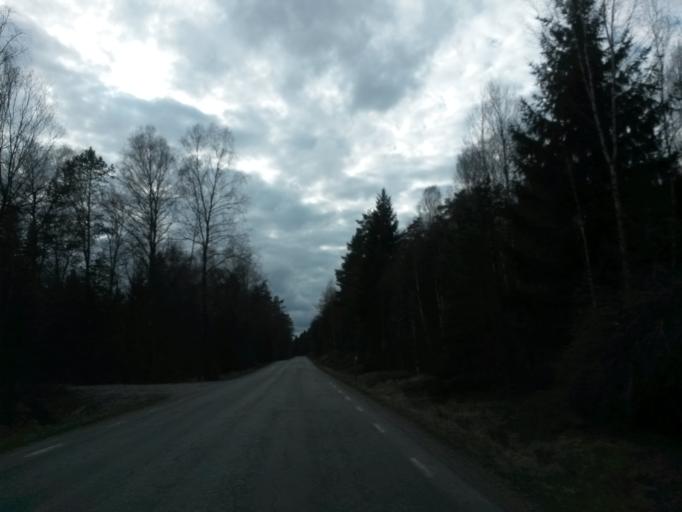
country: SE
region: Vaestra Goetaland
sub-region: Vargarda Kommun
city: Jonstorp
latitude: 57.9479
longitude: 12.6541
